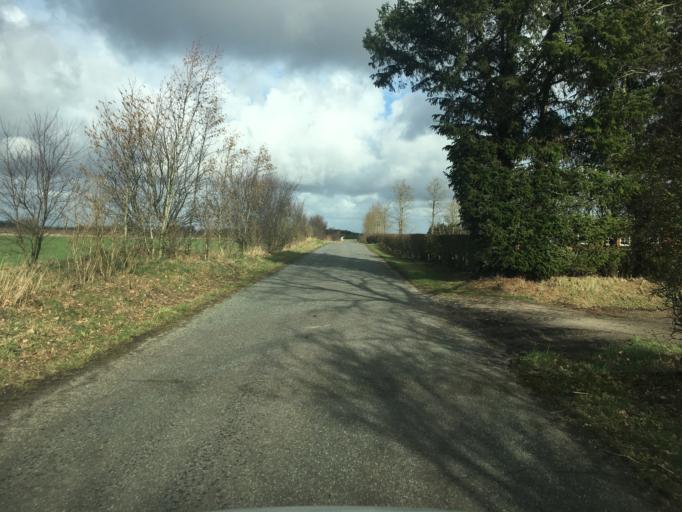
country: DK
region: South Denmark
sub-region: Aabenraa Kommune
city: Krusa
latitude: 54.9161
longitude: 9.3573
